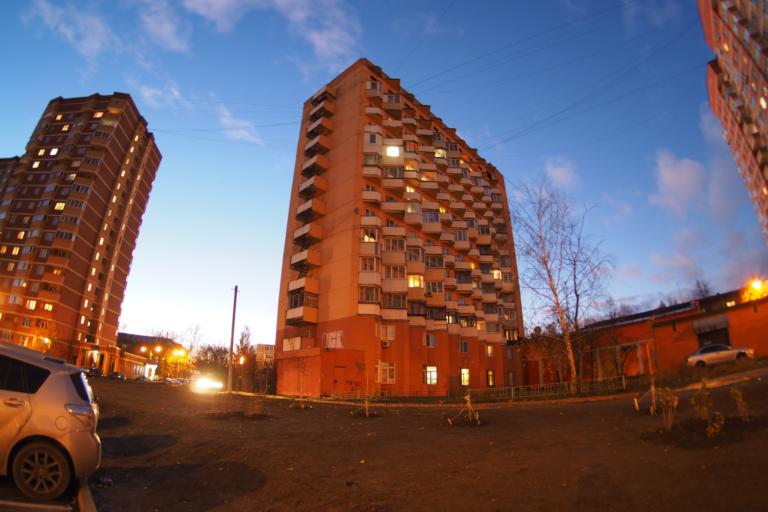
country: RU
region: Moskovskaya
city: Lobnya
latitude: 56.0191
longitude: 37.4238
